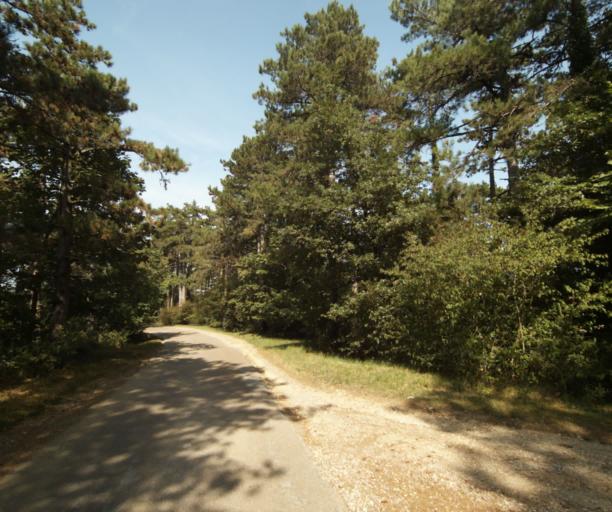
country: FR
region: Bourgogne
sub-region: Departement de Saone-et-Loire
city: Tournus
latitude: 46.5840
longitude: 4.8944
